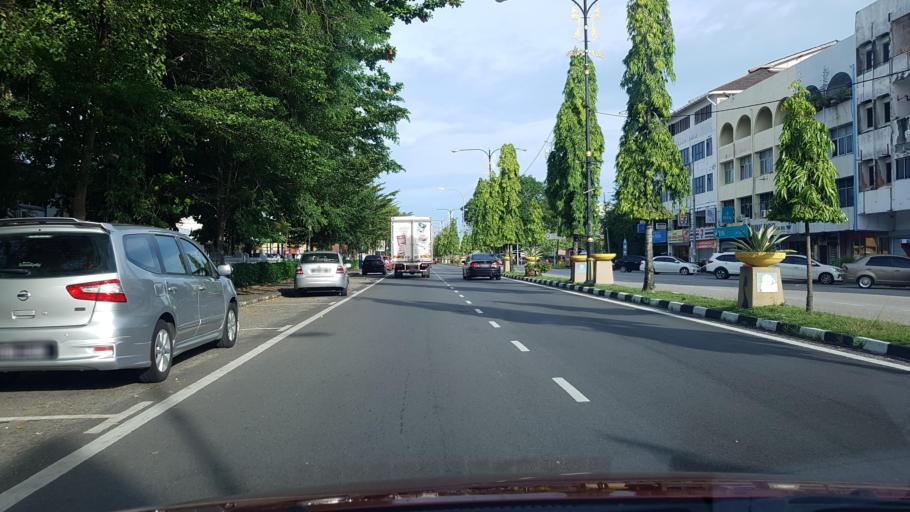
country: MY
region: Terengganu
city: Kuala Terengganu
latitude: 5.3267
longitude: 103.1477
